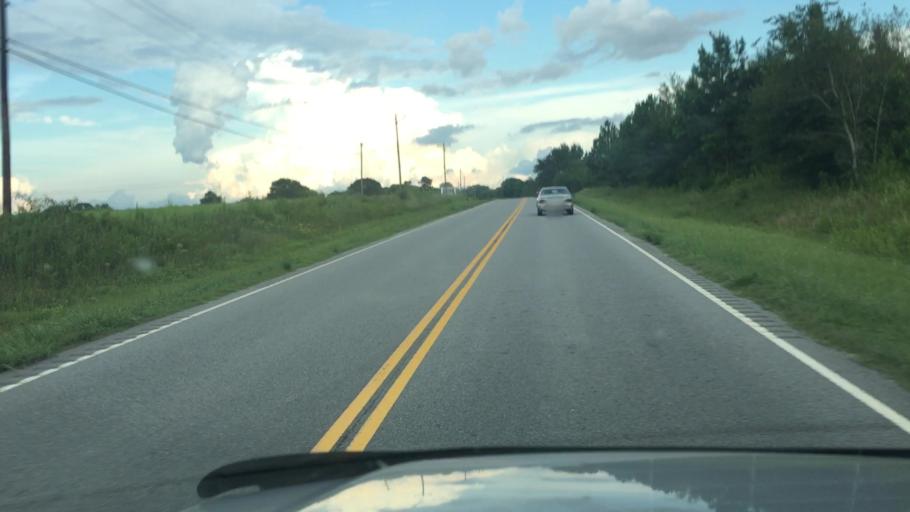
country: US
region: South Carolina
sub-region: Spartanburg County
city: Mayo
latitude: 35.1337
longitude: -81.8011
